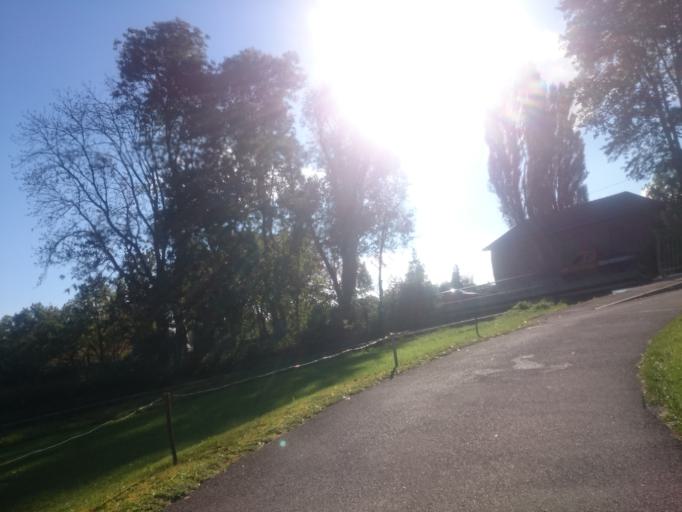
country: DE
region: Bavaria
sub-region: Swabia
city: Augsburg
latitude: 48.3629
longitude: 10.9243
